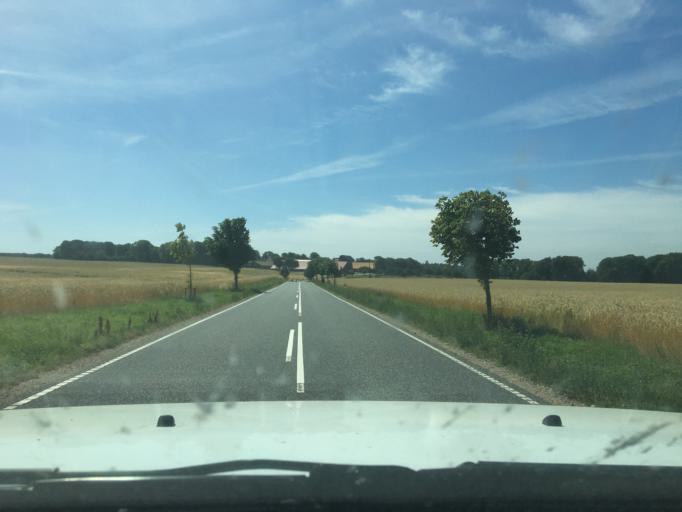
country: DK
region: Central Jutland
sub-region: Viborg Kommune
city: Bjerringbro
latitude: 56.5154
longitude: 9.6222
